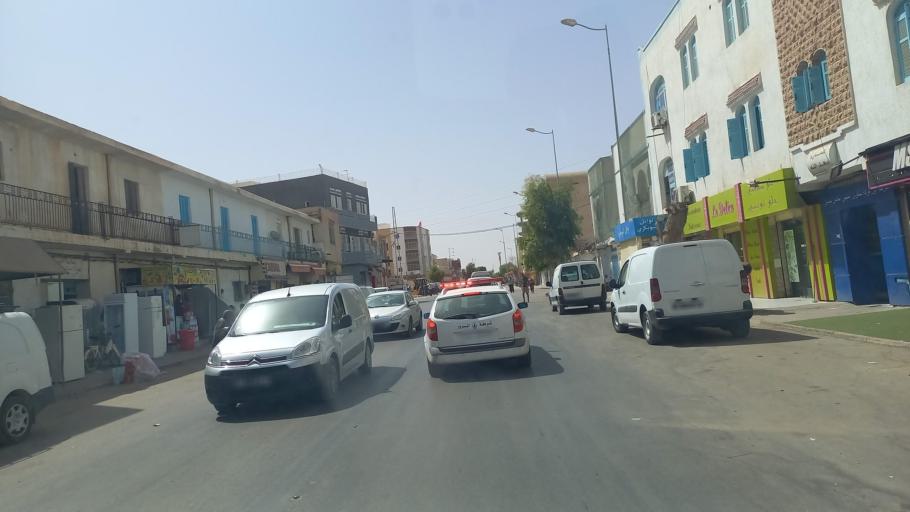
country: TN
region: Madanin
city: Medenine
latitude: 33.3335
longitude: 10.4855
